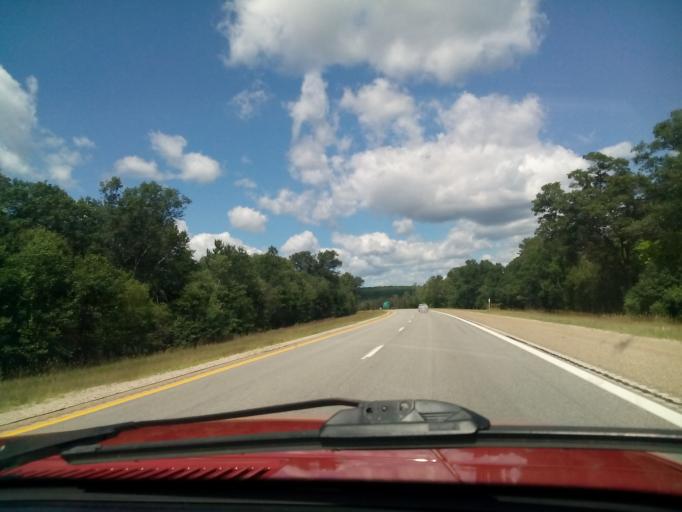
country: US
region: Michigan
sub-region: Roscommon County
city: Roscommon
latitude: 44.4359
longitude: -84.5958
